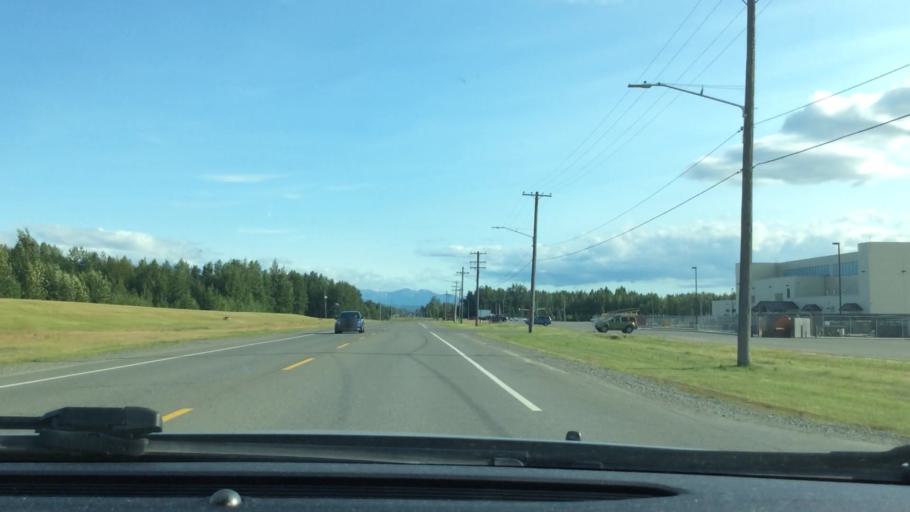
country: US
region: Alaska
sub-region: Anchorage Municipality
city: Anchorage
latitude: 61.2448
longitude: -149.7786
